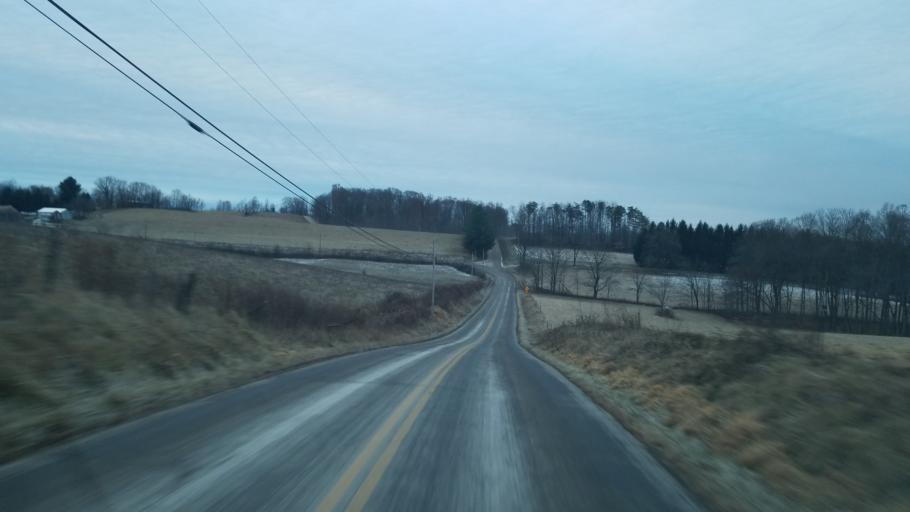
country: US
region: Ohio
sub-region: Holmes County
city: Millersburg
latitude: 40.4923
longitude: -81.8827
